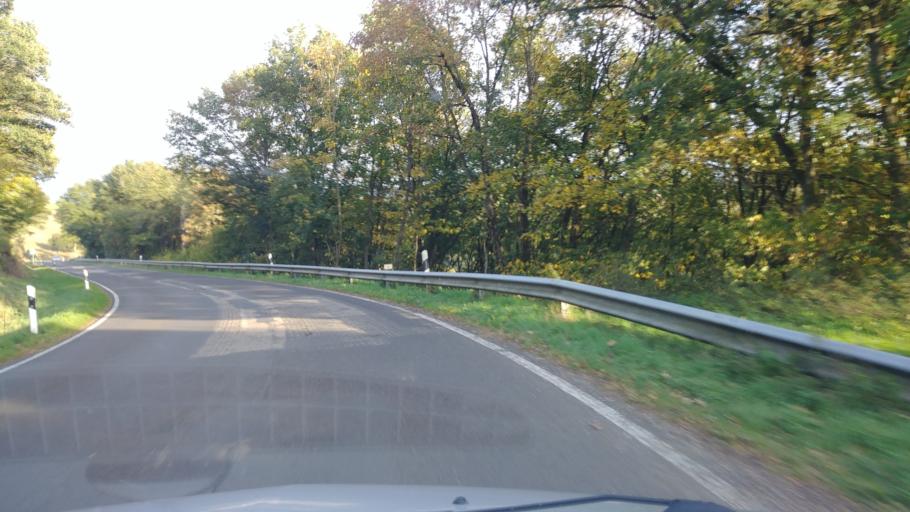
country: DE
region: Rheinland-Pfalz
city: Gornhausen
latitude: 49.8192
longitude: 7.0658
